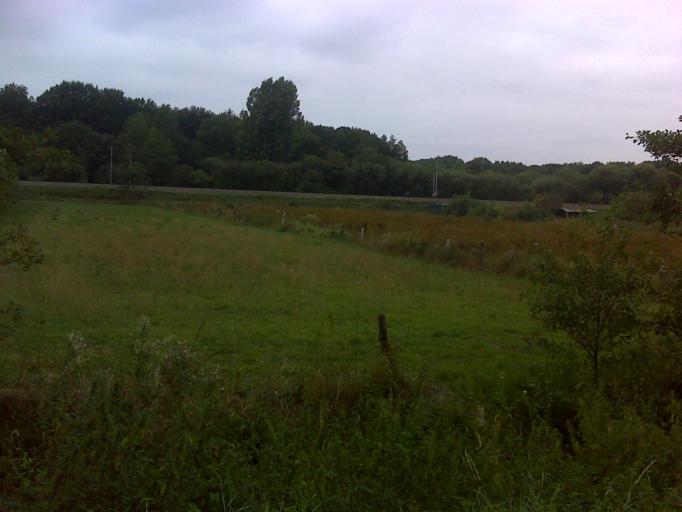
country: FR
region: Nord-Pas-de-Calais
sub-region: Departement du Nord
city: Landrecies
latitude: 50.1115
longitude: 3.6487
